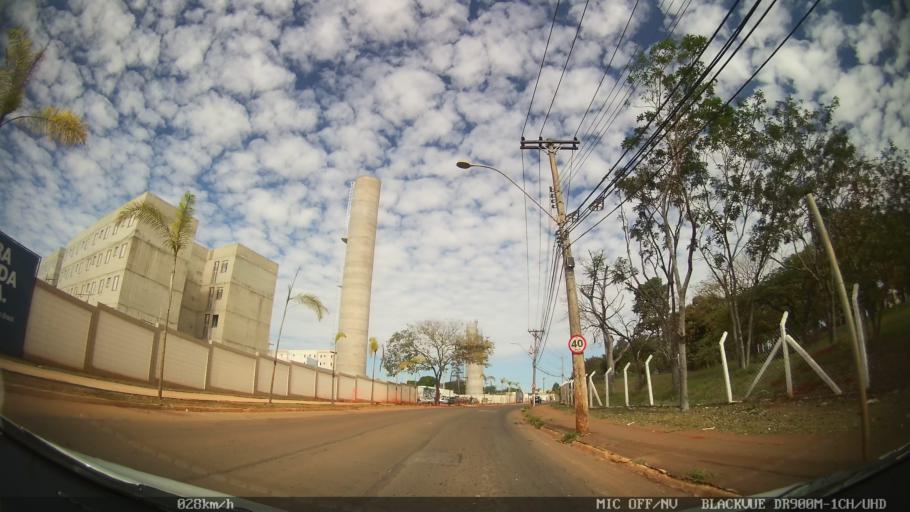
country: BR
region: Sao Paulo
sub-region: Santa Barbara D'Oeste
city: Santa Barbara d'Oeste
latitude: -22.7670
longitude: -47.4042
